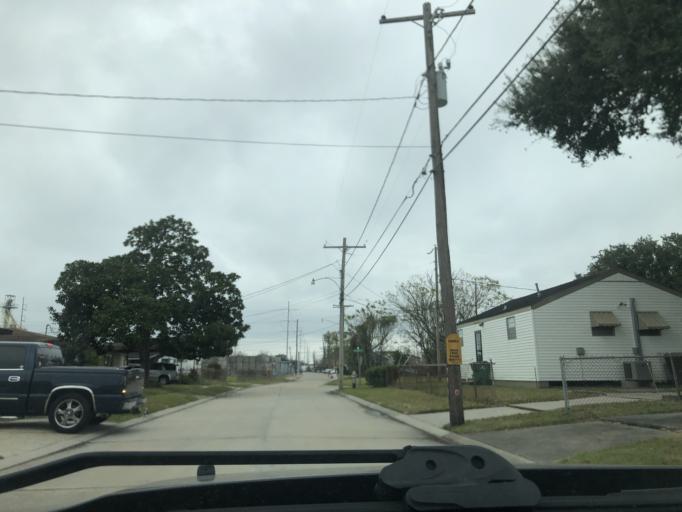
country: US
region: Louisiana
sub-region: Jefferson Parish
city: Metairie Terrace
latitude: 29.9726
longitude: -90.1643
